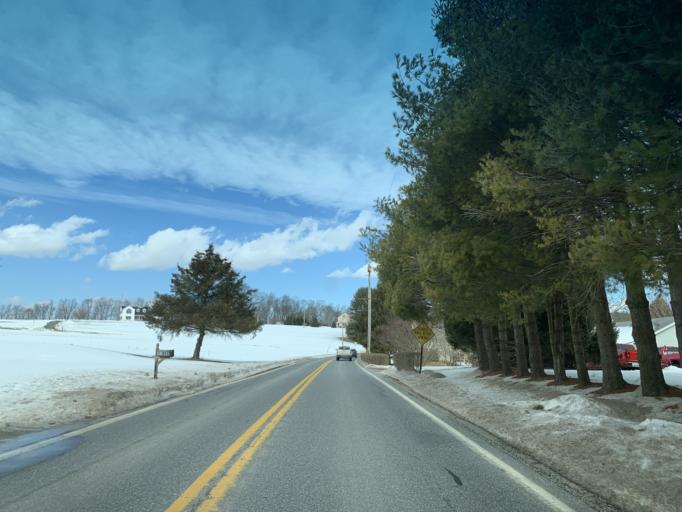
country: US
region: Pennsylvania
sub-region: York County
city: Shrewsbury
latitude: 39.8215
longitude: -76.6291
